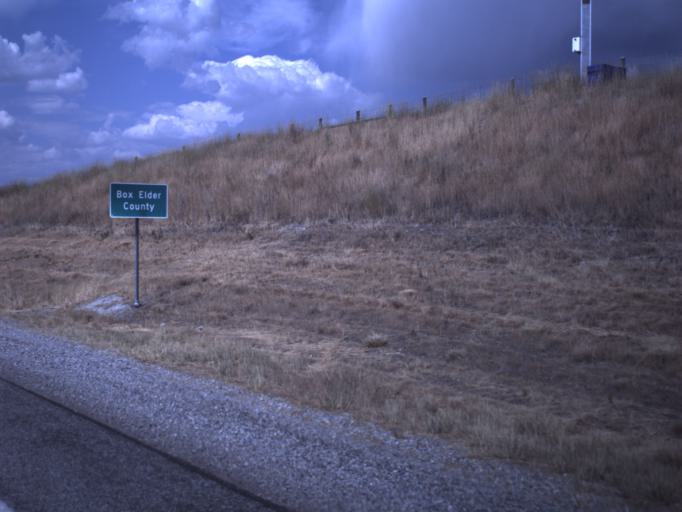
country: US
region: Utah
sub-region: Cache County
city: Mendon
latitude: 41.7788
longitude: -112.0219
